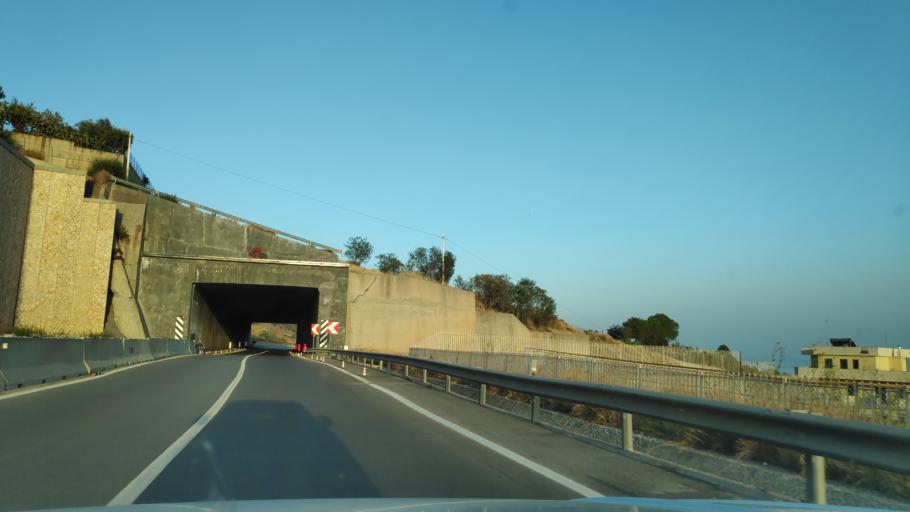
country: IT
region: Calabria
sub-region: Provincia di Reggio Calabria
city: Bova Marina
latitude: 37.9345
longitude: 15.9197
